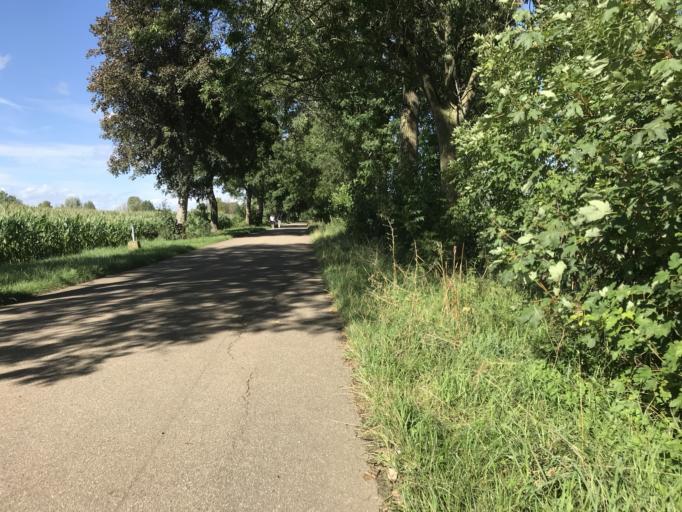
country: DE
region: Baden-Wuerttemberg
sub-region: Tuebingen Region
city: Langenau
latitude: 48.4769
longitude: 10.1267
